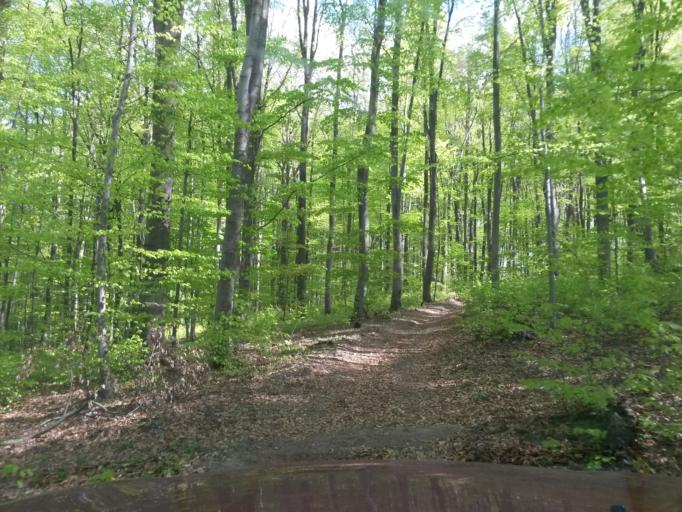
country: SK
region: Presovsky
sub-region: Okres Presov
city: Presov
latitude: 48.9436
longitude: 21.1356
